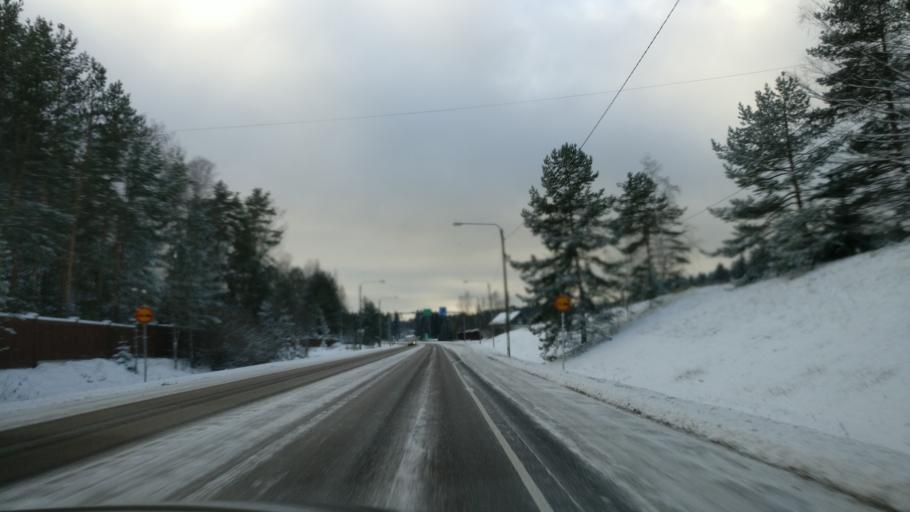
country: FI
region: Paijanne Tavastia
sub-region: Lahti
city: Heinola
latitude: 61.3345
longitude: 26.1712
